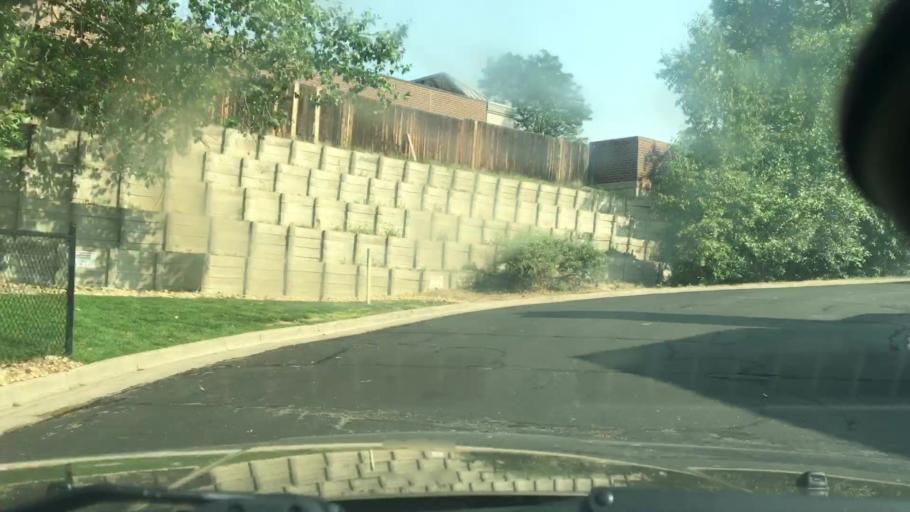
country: US
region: Colorado
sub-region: Douglas County
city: Acres Green
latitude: 39.5667
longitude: -104.9080
